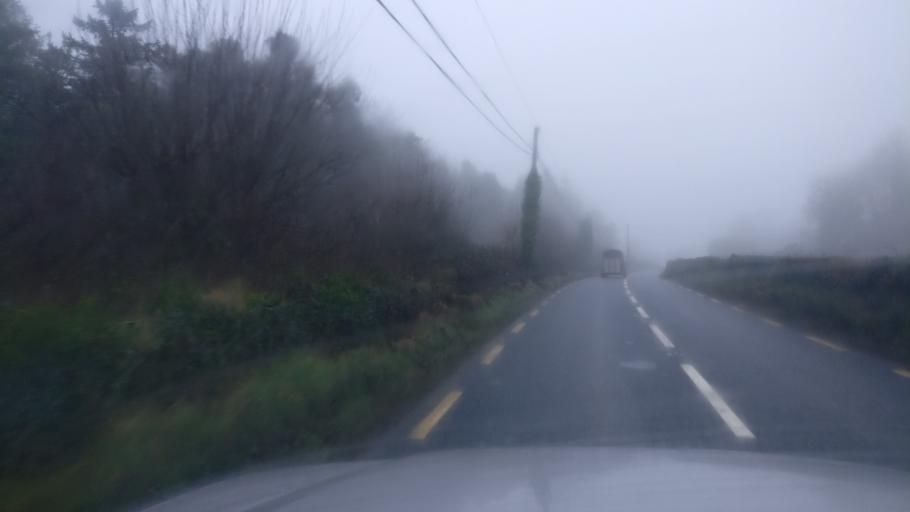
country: IE
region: Connaught
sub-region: County Galway
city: Loughrea
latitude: 53.1697
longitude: -8.6695
